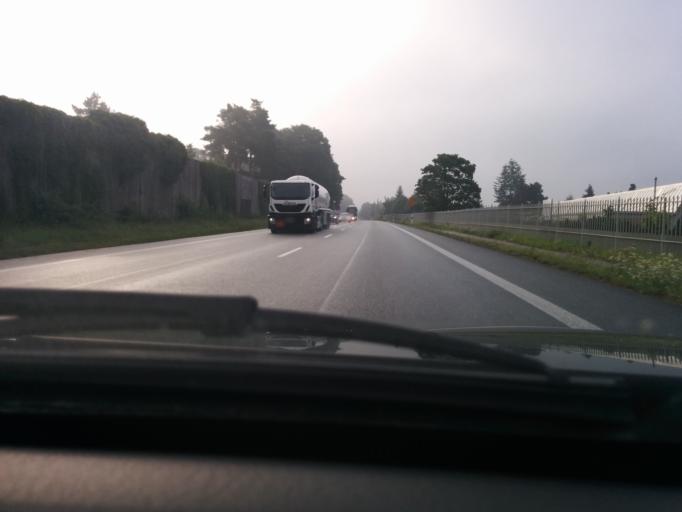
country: DE
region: North Rhine-Westphalia
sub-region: Regierungsbezirk Detmold
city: Steinhagen
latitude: 52.0208
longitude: 8.4288
